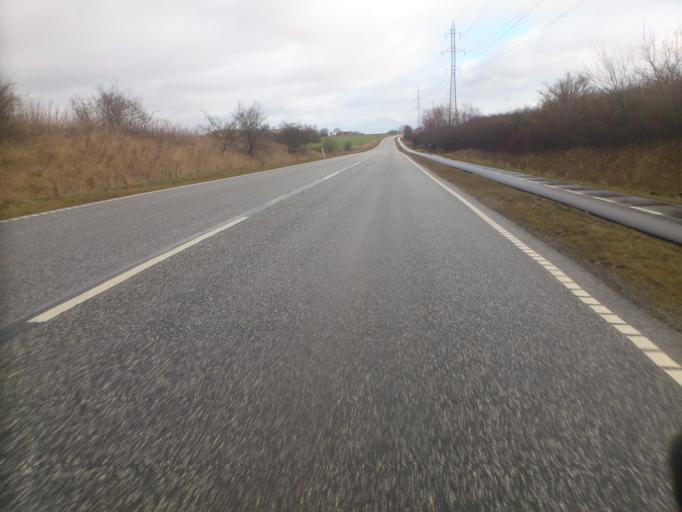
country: DK
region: South Denmark
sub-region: Fredericia Kommune
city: Fredericia
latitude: 55.5937
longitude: 9.7241
